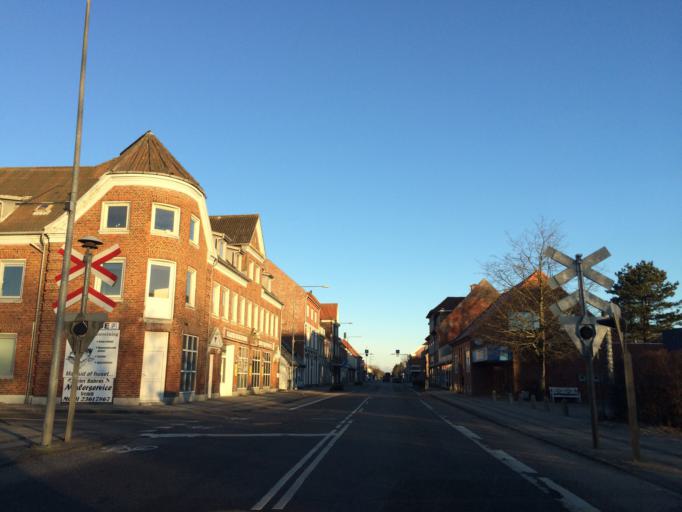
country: DK
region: Central Jutland
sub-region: Holstebro Kommune
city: Ulfborg
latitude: 56.3426
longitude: 8.3441
